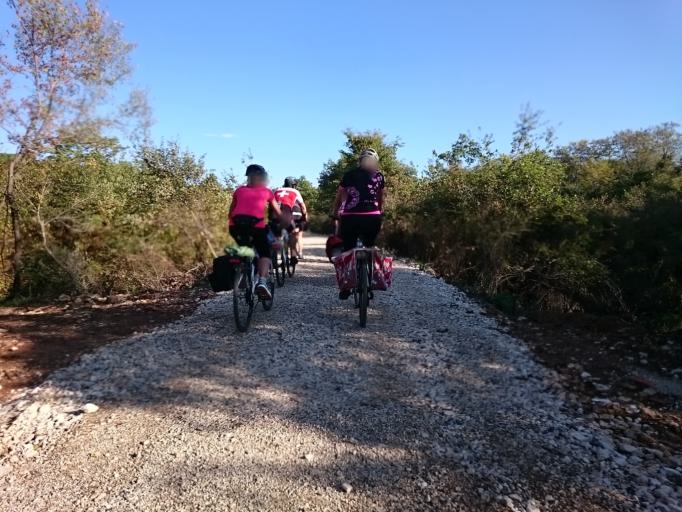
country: HR
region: Istarska
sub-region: Grad Porec
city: Porec
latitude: 45.2386
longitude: 13.6115
